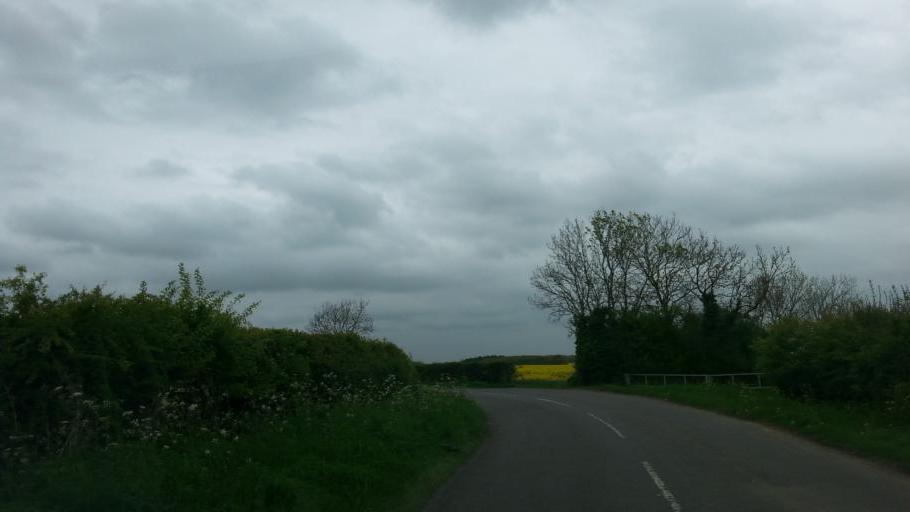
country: GB
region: England
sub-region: Lincolnshire
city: Grantham
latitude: 52.8662
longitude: -0.5197
